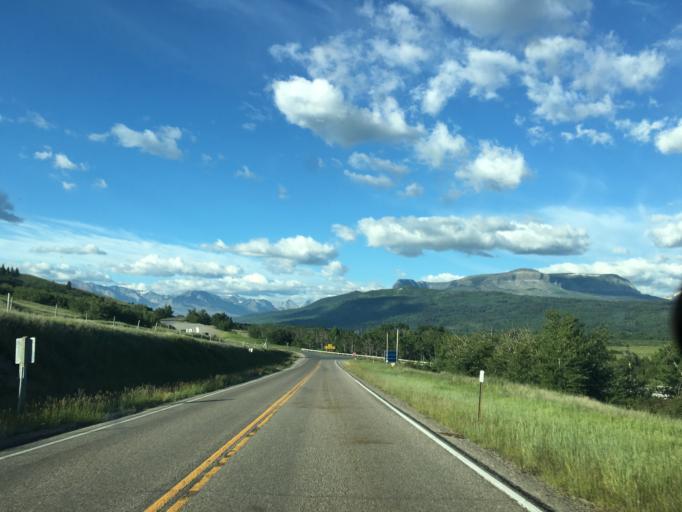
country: CA
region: Alberta
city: Cardston
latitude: 48.8449
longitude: -113.4161
